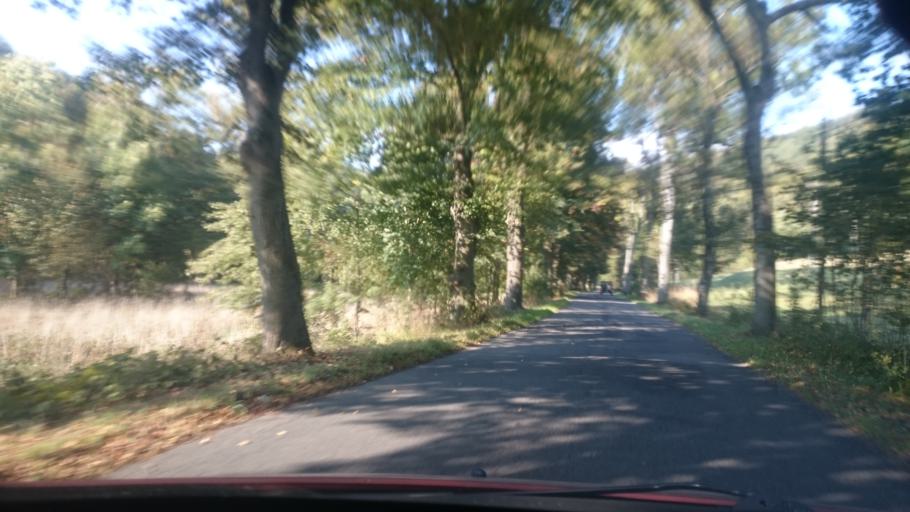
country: PL
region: Lower Silesian Voivodeship
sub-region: Powiat klodzki
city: Bystrzyca Klodzka
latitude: 50.3028
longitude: 16.5813
